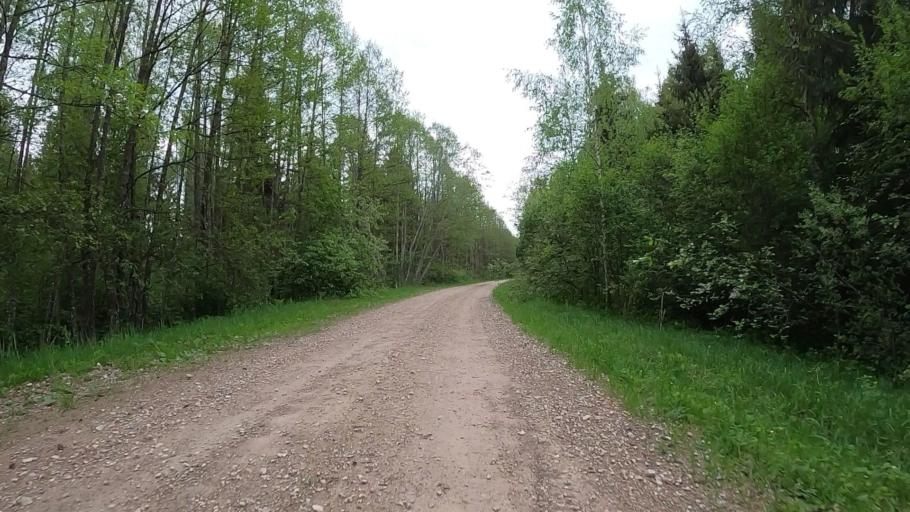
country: LV
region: Ozolnieku
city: Ozolnieki
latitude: 56.8012
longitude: 23.7841
